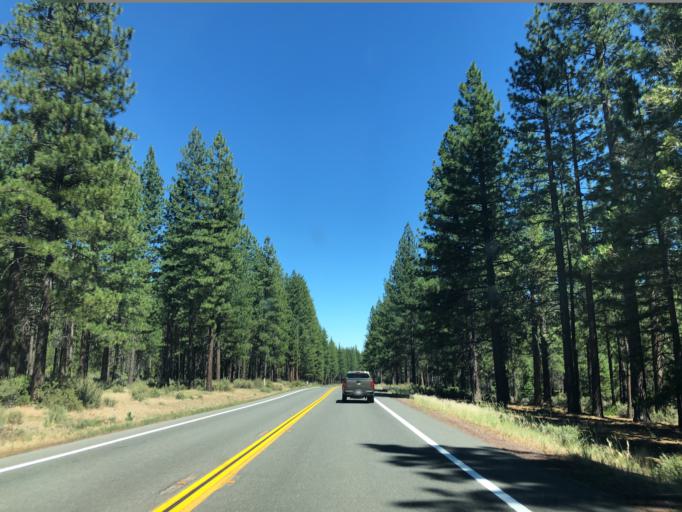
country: US
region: California
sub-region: Lassen County
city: Susanville
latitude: 40.4167
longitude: -120.7689
